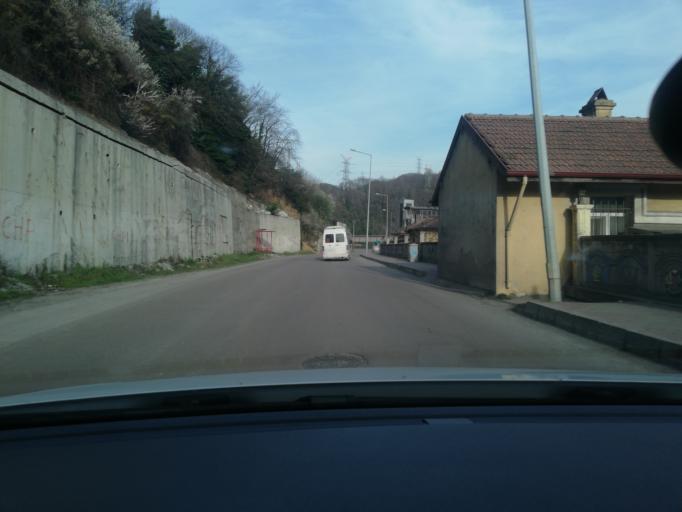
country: TR
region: Zonguldak
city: Kilimli
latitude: 41.5001
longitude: 31.8781
